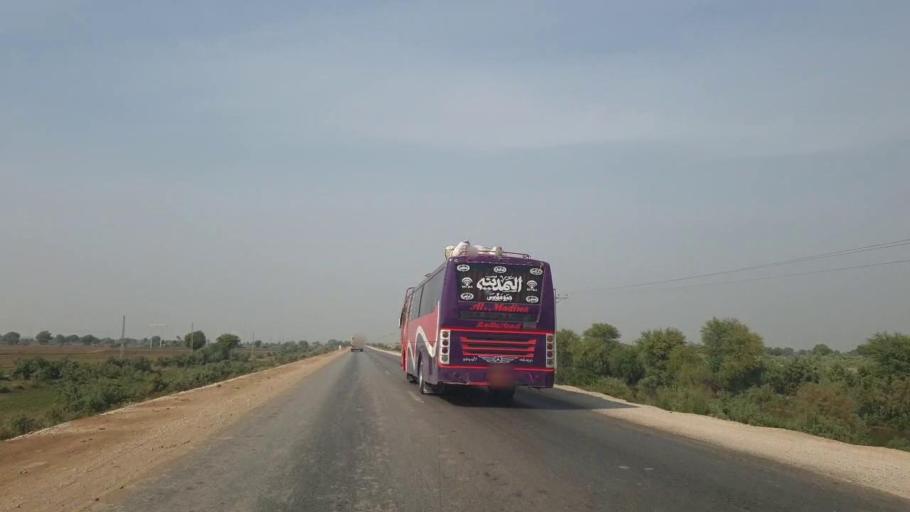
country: PK
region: Sindh
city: Sann
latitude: 26.0778
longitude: 68.0958
